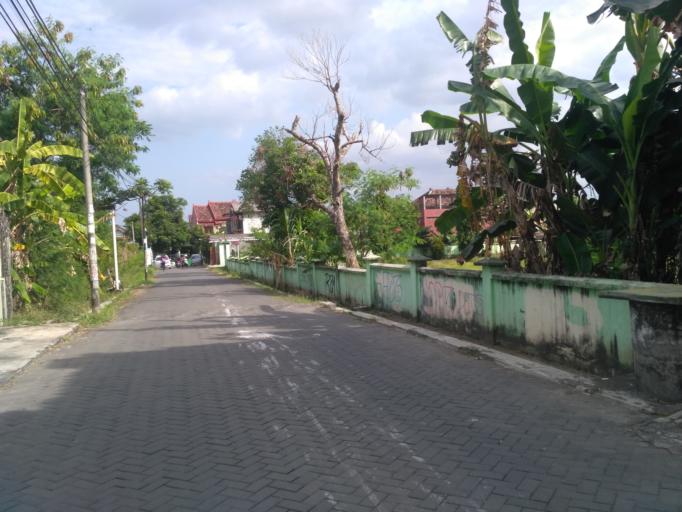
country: ID
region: Daerah Istimewa Yogyakarta
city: Depok
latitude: -7.7797
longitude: 110.4114
